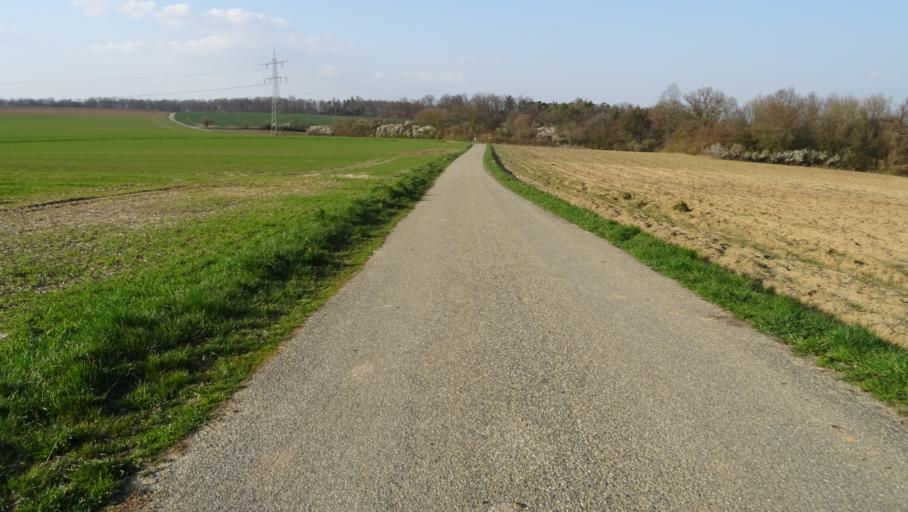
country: DE
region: Baden-Wuerttemberg
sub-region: Regierungsbezirk Stuttgart
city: Roigheim
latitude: 49.3807
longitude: 9.3577
